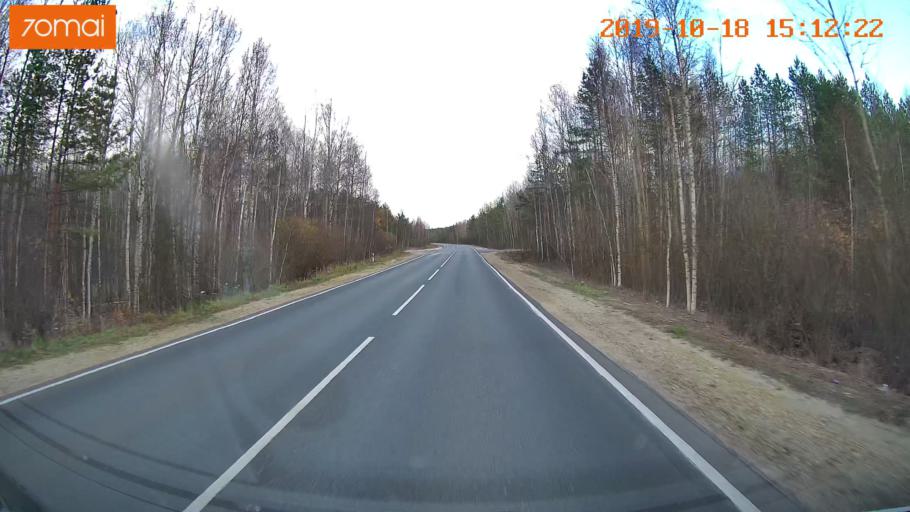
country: RU
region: Vladimir
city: Gus'-Khrustal'nyy
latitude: 55.5758
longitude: 40.6960
